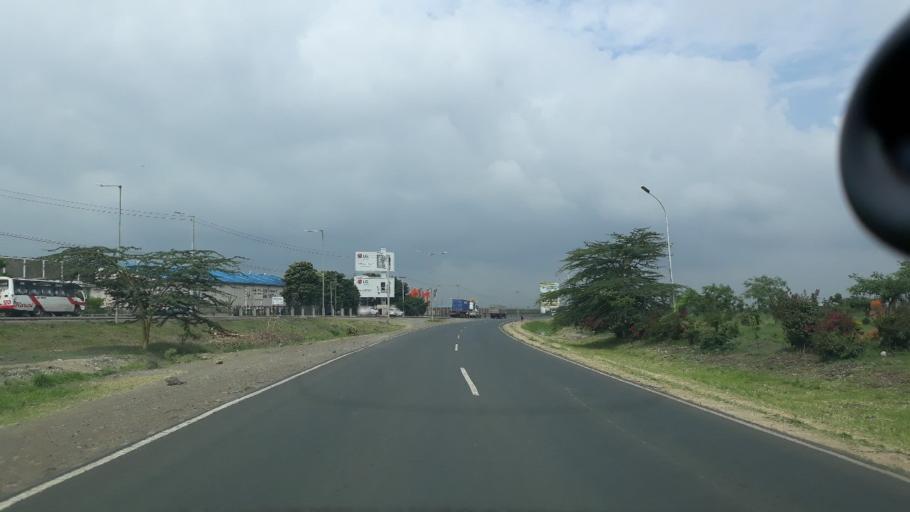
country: KE
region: Nairobi Area
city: Pumwani
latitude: -1.3474
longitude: 36.9037
